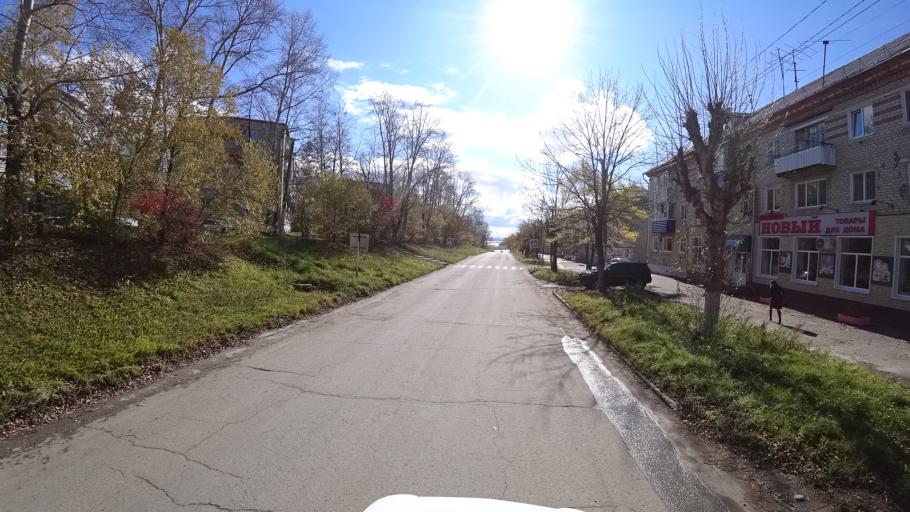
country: RU
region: Khabarovsk Krai
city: Amursk
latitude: 50.2178
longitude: 136.9032
